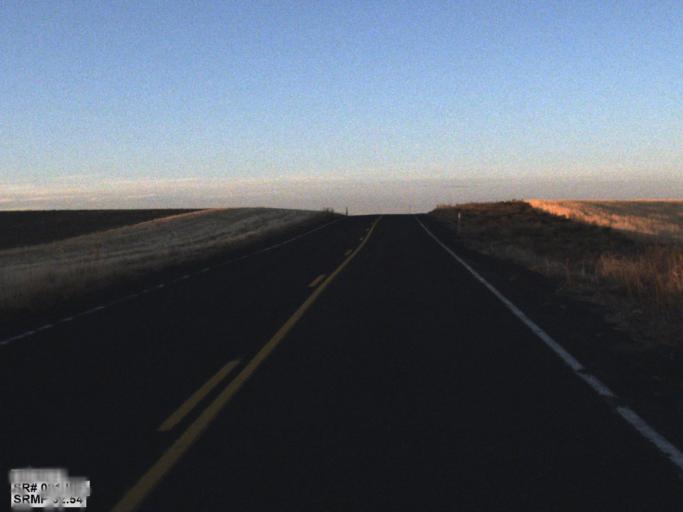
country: US
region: Washington
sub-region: Adams County
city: Ritzville
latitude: 47.0215
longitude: -118.6635
